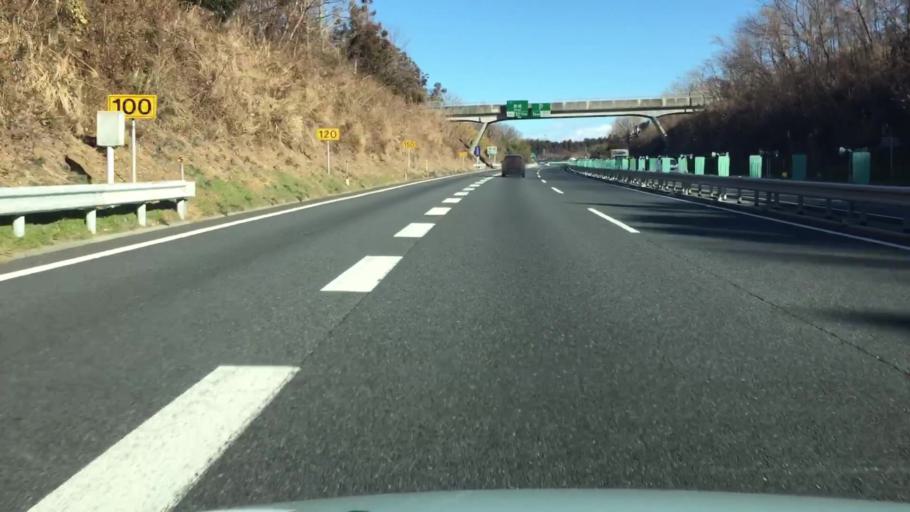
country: JP
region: Gunma
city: Shibukawa
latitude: 36.5273
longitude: 139.0418
